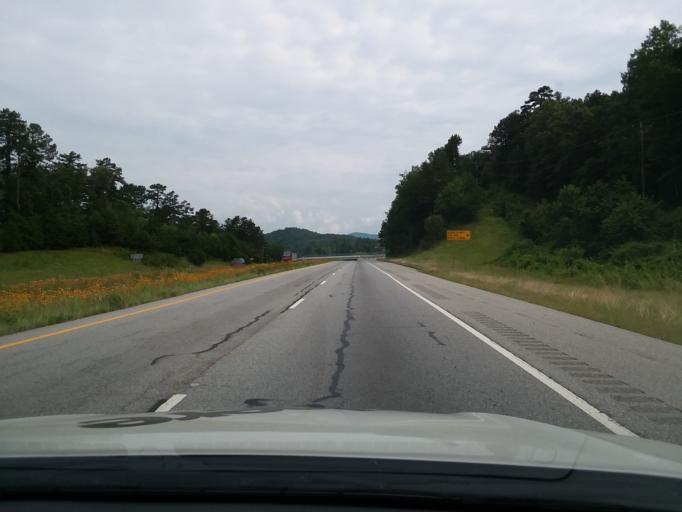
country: US
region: Georgia
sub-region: Rabun County
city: Clayton
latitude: 34.8229
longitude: -83.4238
